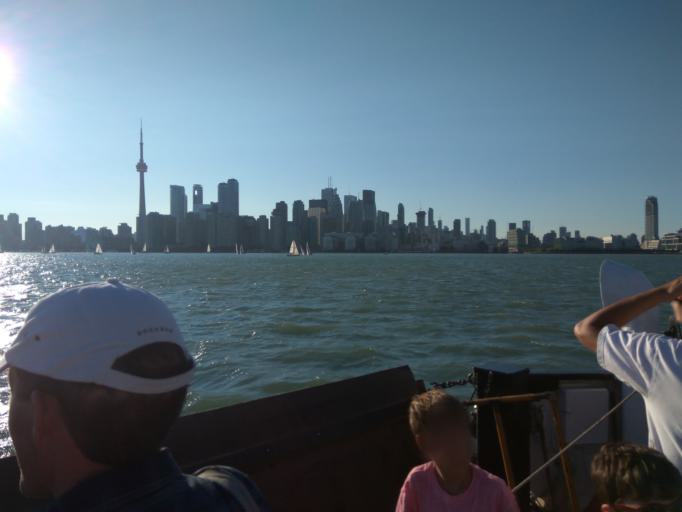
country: CA
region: Ontario
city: Toronto
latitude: 43.6313
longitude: -79.3625
